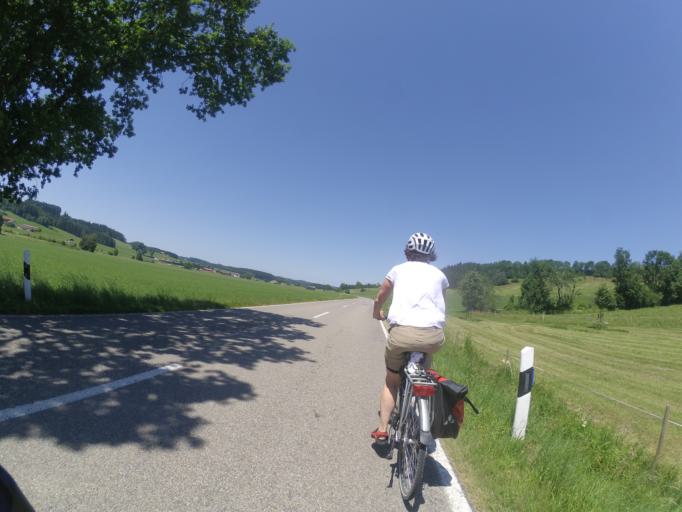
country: DE
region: Bavaria
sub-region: Swabia
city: Bohen
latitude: 47.8770
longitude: 10.3366
